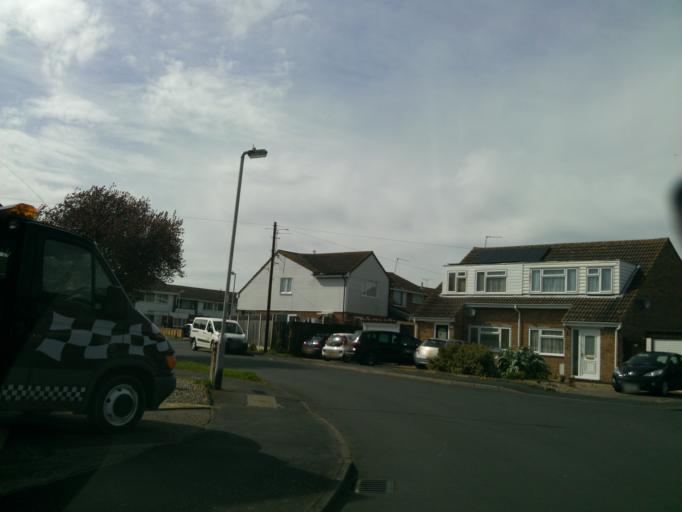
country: GB
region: England
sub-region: Essex
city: Witham
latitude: 51.8465
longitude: 0.6302
